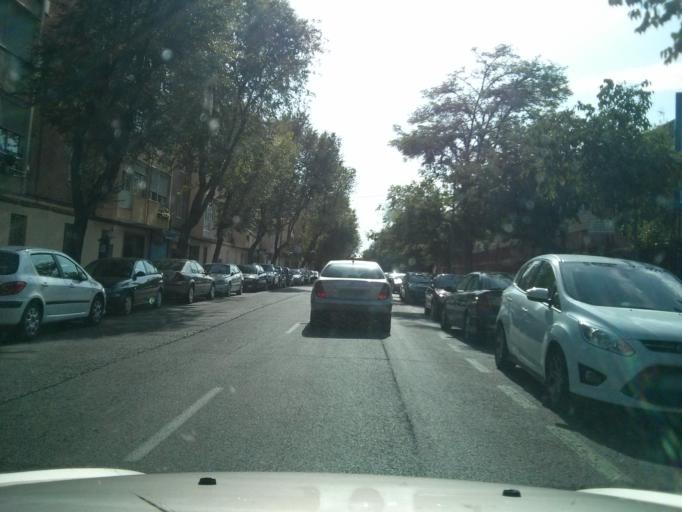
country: ES
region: Madrid
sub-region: Provincia de Madrid
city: Tetuan de las Victorias
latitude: 40.4733
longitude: -3.7127
